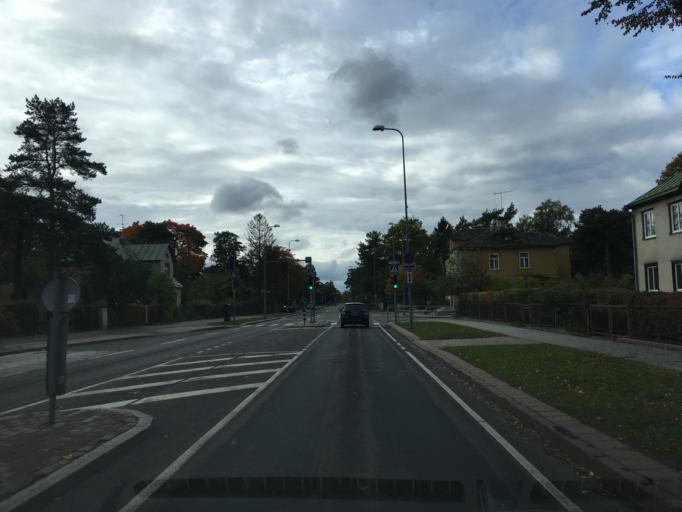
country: EE
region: Harju
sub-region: Saue vald
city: Laagri
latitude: 59.3764
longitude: 24.6500
